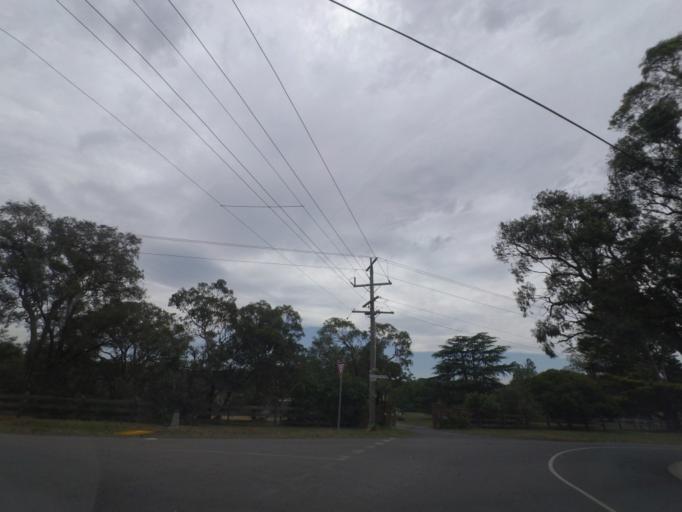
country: AU
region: Victoria
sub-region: Nillumbik
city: Diamond Creek
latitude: -37.6735
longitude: 145.1343
